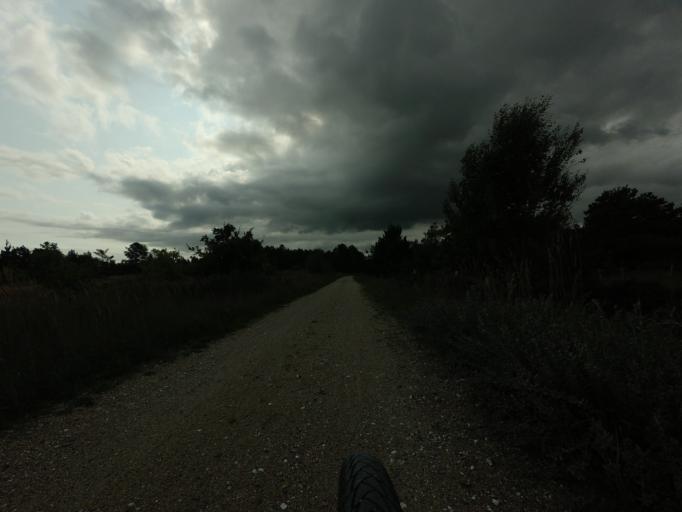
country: DK
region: North Denmark
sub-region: Frederikshavn Kommune
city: Strandby
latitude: 57.6288
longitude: 10.4020
